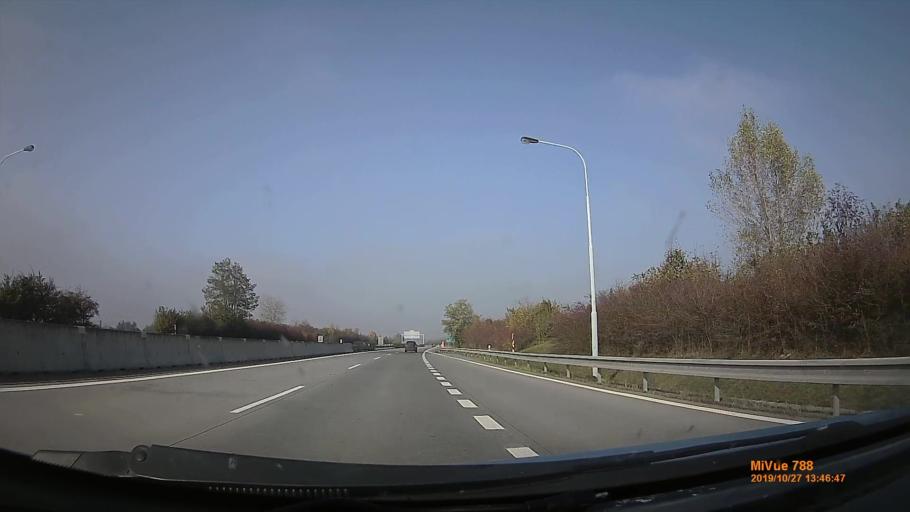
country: CZ
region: Olomoucky
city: Hnevotin
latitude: 49.5770
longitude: 17.2088
